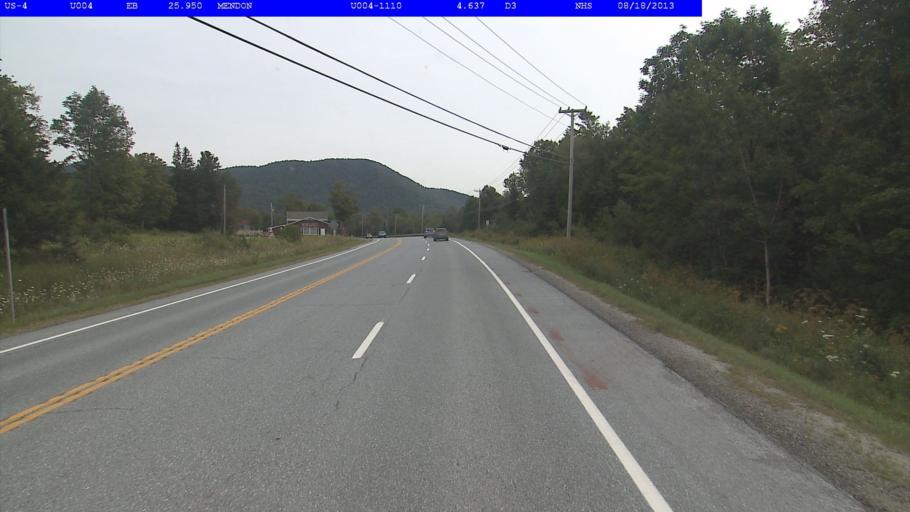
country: US
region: Vermont
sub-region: Rutland County
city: Rutland
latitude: 43.6607
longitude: -72.8671
